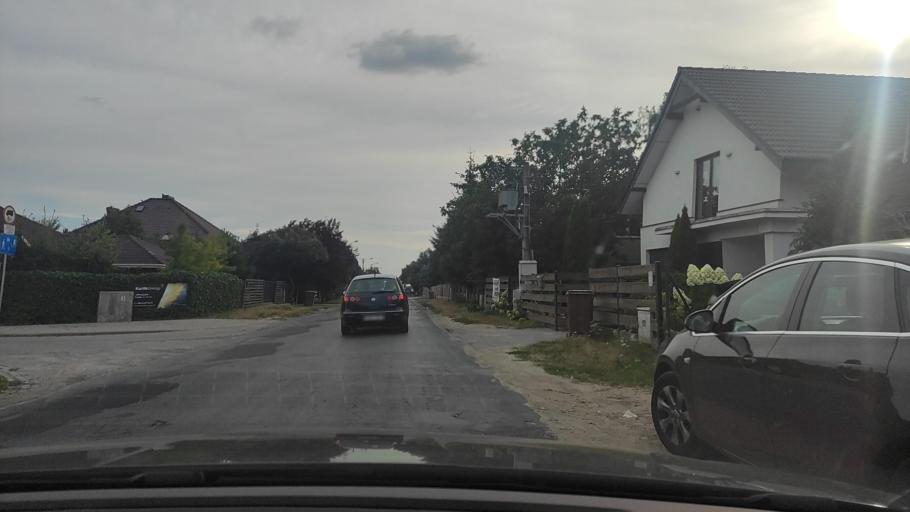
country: PL
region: Greater Poland Voivodeship
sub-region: Powiat poznanski
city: Kleszczewo
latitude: 52.3635
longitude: 17.1355
